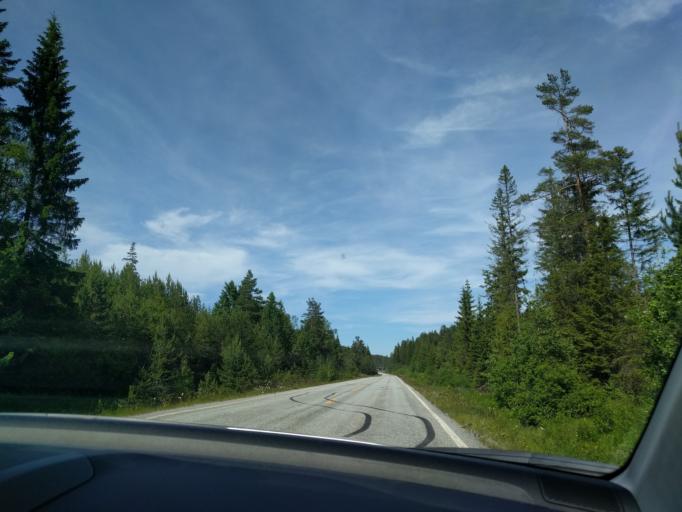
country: NO
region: Aust-Agder
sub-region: Gjerstad
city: Gjerstad
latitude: 58.8648
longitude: 9.1479
